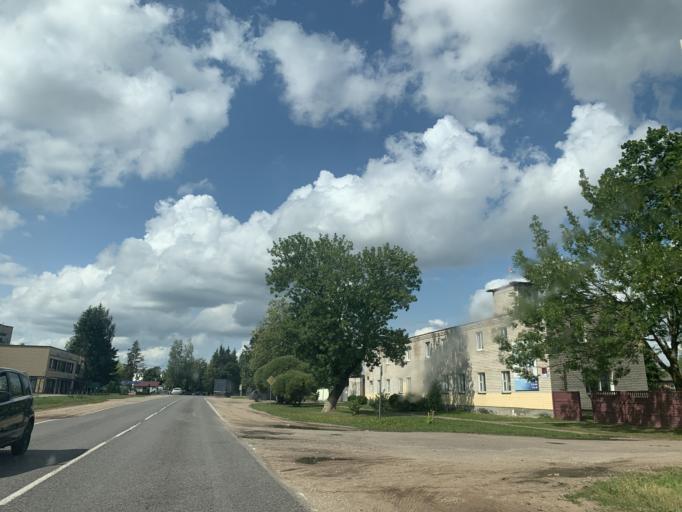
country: BY
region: Minsk
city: Enyerhyetykaw
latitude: 53.5837
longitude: 27.0535
